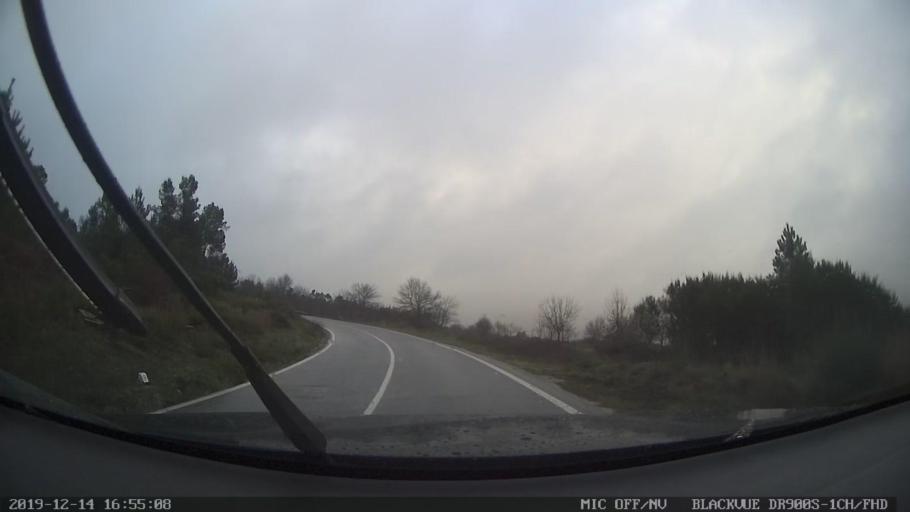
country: PT
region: Vila Real
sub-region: Murca
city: Murca
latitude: 41.4391
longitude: -7.5281
